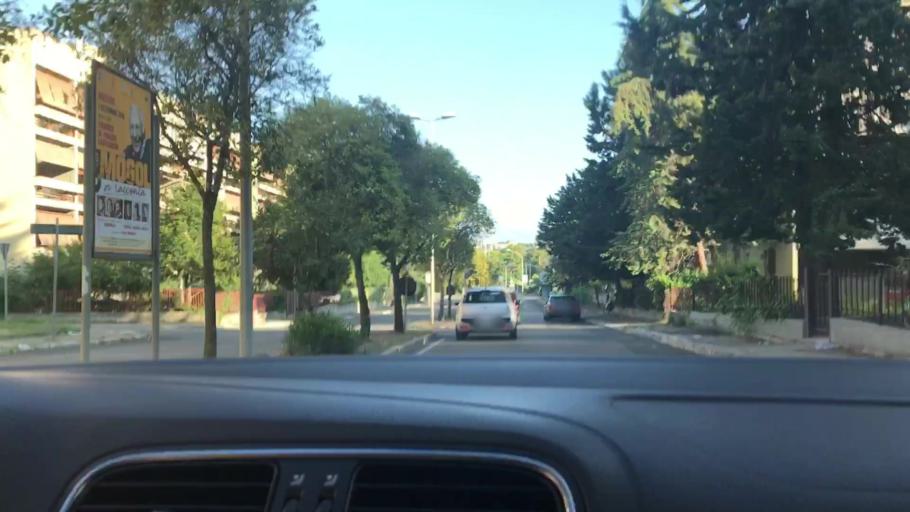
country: IT
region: Basilicate
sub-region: Provincia di Matera
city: Matera
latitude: 40.6823
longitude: 16.5863
